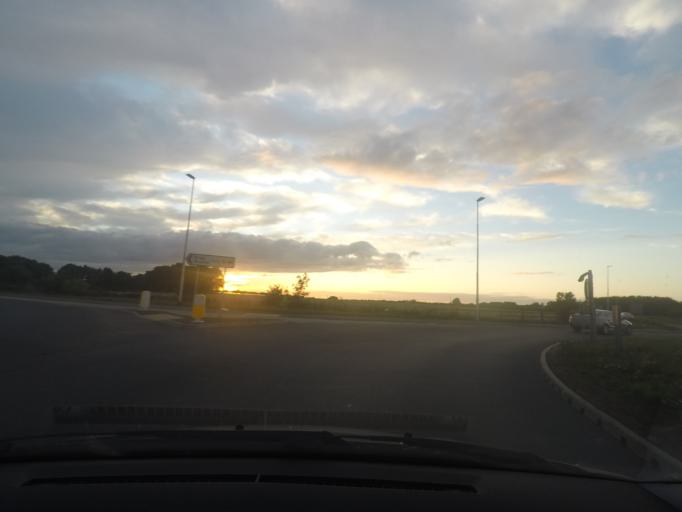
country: GB
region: England
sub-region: North Lincolnshire
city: Barnetby le Wold
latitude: 53.5823
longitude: -0.4114
